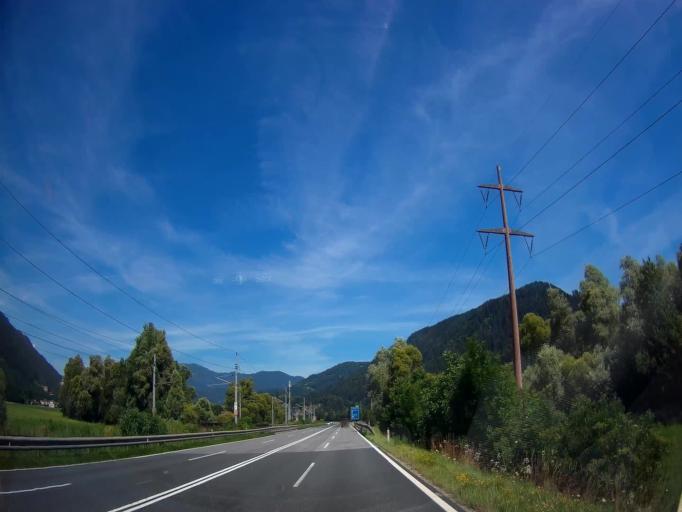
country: AT
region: Carinthia
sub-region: Politischer Bezirk Sankt Veit an der Glan
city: Friesach
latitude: 46.9413
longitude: 14.4240
